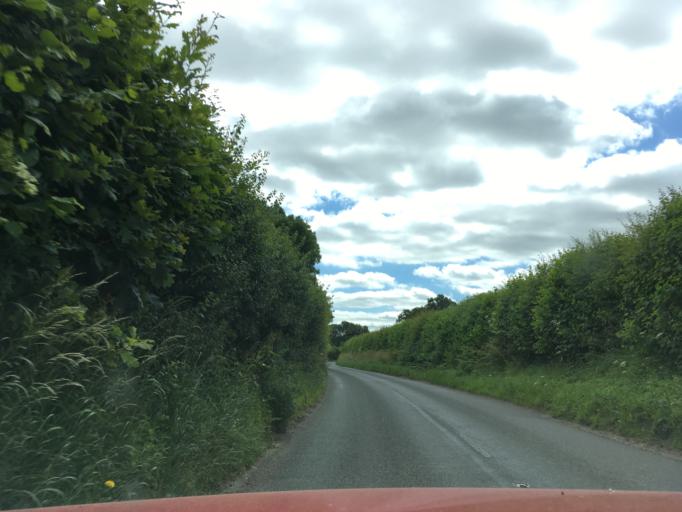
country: GB
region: England
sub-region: West Berkshire
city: Welford
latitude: 51.4311
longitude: -1.3829
